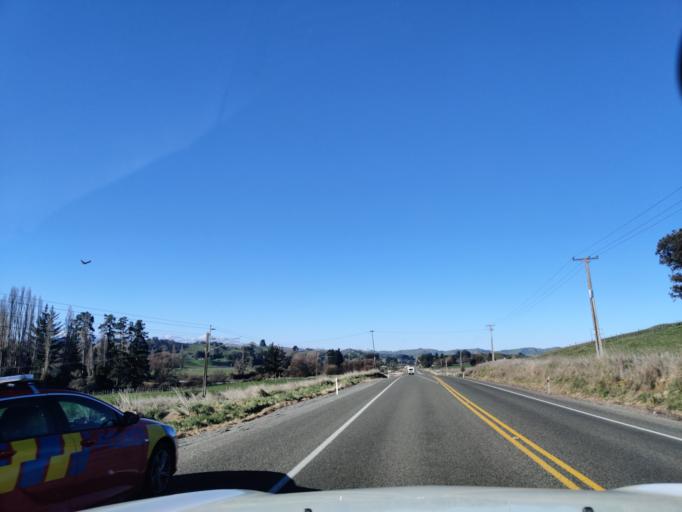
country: NZ
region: Manawatu-Wanganui
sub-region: Ruapehu District
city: Waiouru
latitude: -39.7162
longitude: 175.8395
